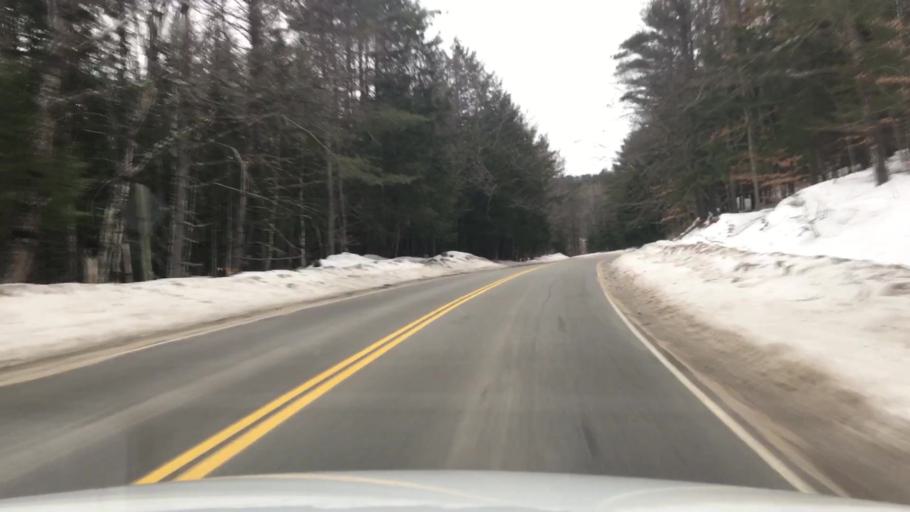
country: US
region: Maine
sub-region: Oxford County
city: Hiram
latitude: 43.8883
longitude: -70.7912
